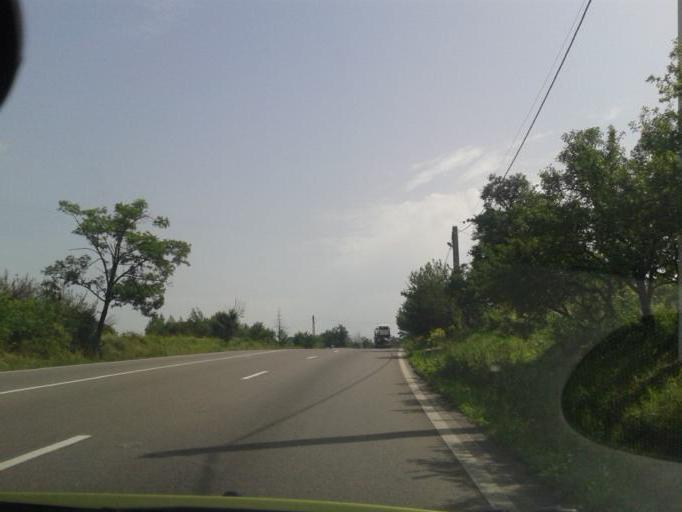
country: RO
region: Arges
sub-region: Comuna Cotmeana
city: Cotmeana
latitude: 45.0001
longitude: 24.6085
